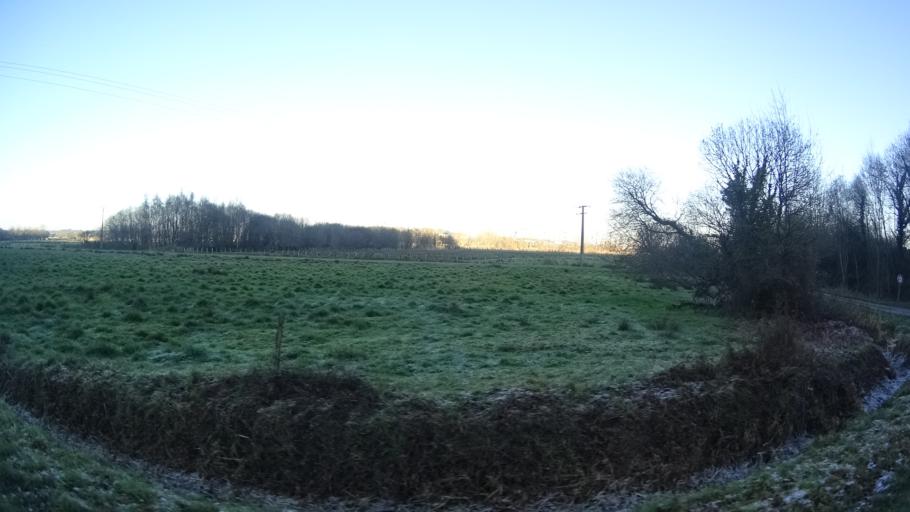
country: FR
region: Brittany
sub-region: Departement du Morbihan
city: Saint-Jean-la-Poterie
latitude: 47.6410
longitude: -2.1140
